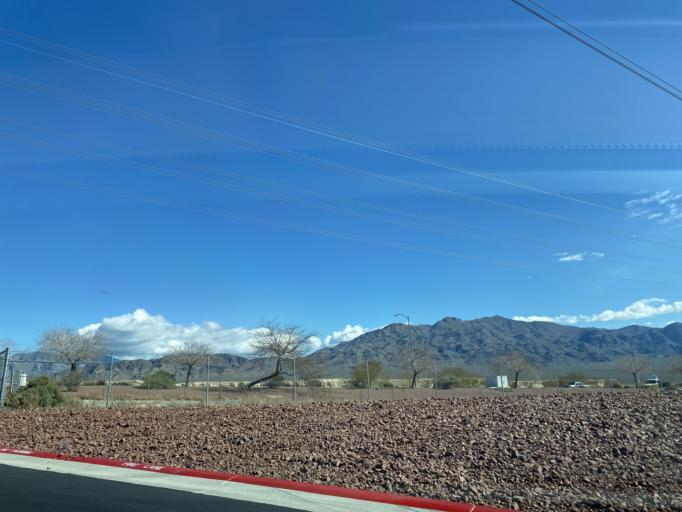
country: US
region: Nevada
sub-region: Clark County
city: North Las Vegas
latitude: 36.3353
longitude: -115.2739
